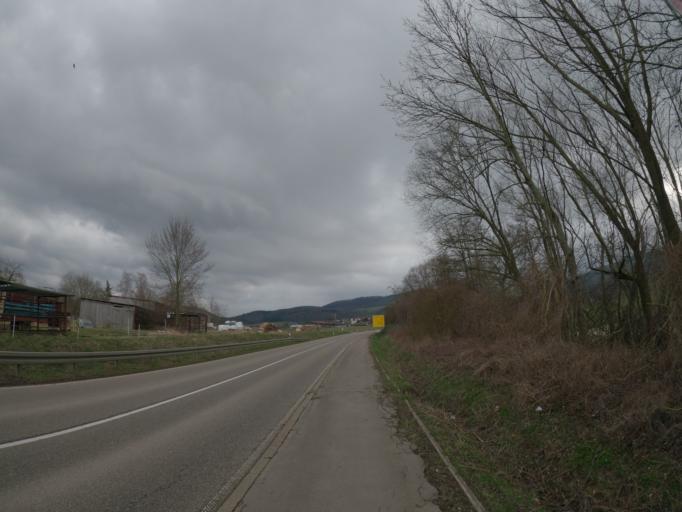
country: DE
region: Baden-Wuerttemberg
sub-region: Regierungsbezirk Stuttgart
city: Schlat
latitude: 48.6606
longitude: 9.7040
